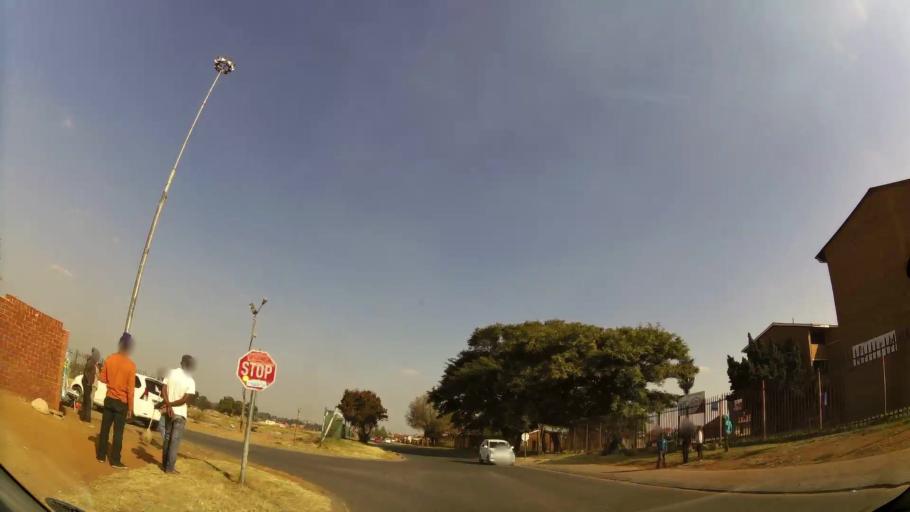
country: ZA
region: Gauteng
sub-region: Ekurhuleni Metropolitan Municipality
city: Benoni
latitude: -26.1553
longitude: 28.4006
